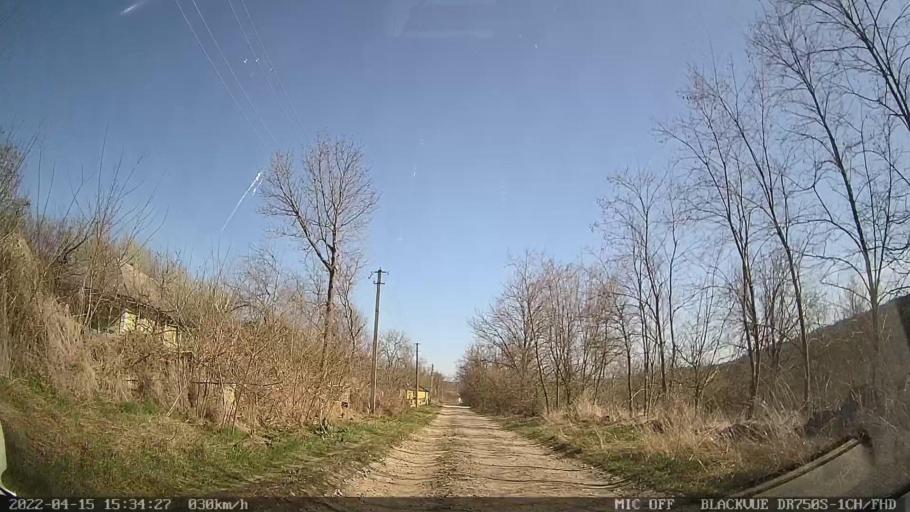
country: MD
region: Raionul Ocnita
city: Otaci
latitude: 48.3474
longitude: 27.9274
